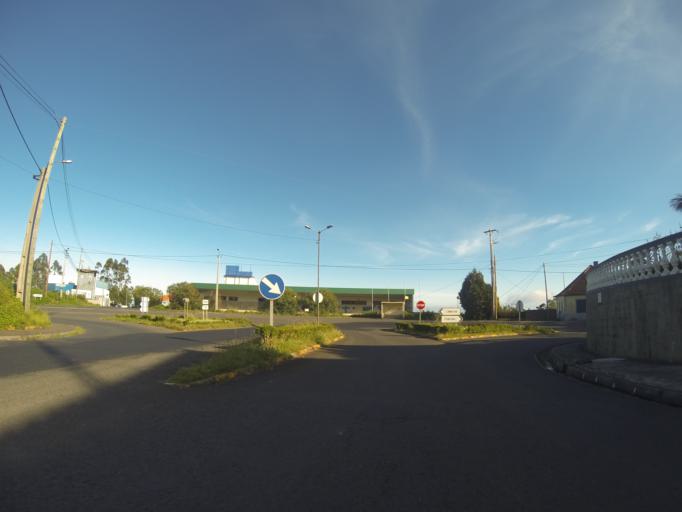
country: PT
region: Madeira
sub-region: Santa Cruz
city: Camacha
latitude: 32.6714
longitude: -16.8631
